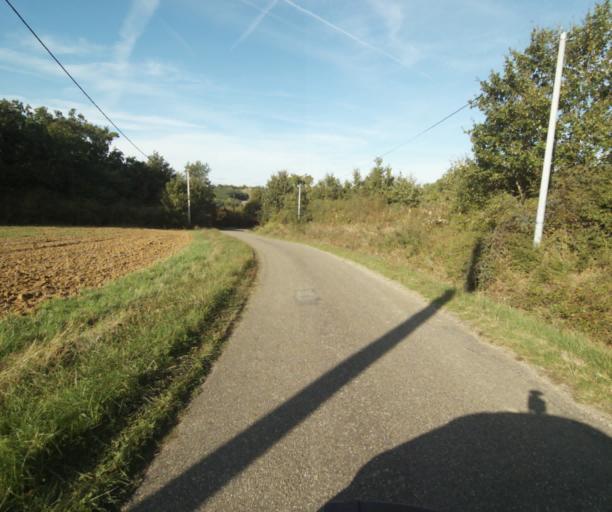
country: FR
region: Midi-Pyrenees
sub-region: Departement du Tarn-et-Garonne
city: Saint-Porquier
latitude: 43.9320
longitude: 1.1432
